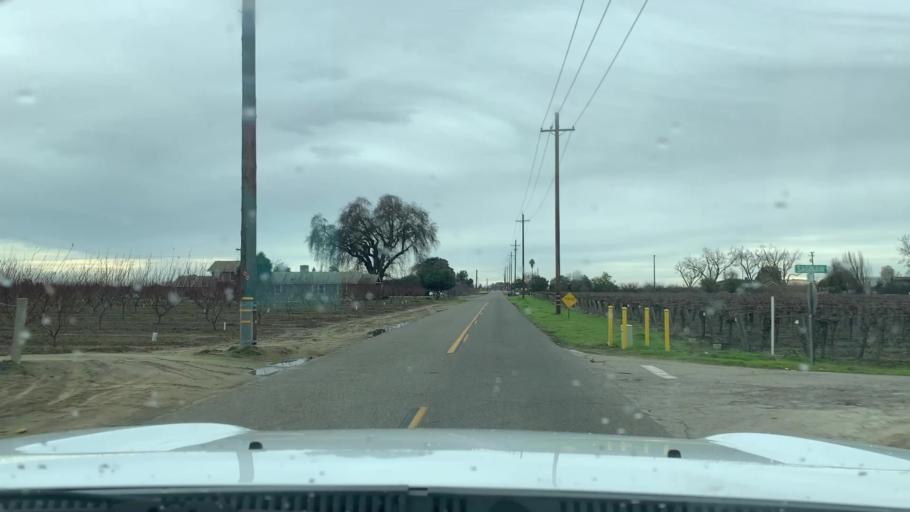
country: US
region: California
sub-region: Fresno County
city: Selma
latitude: 36.5542
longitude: -119.5751
